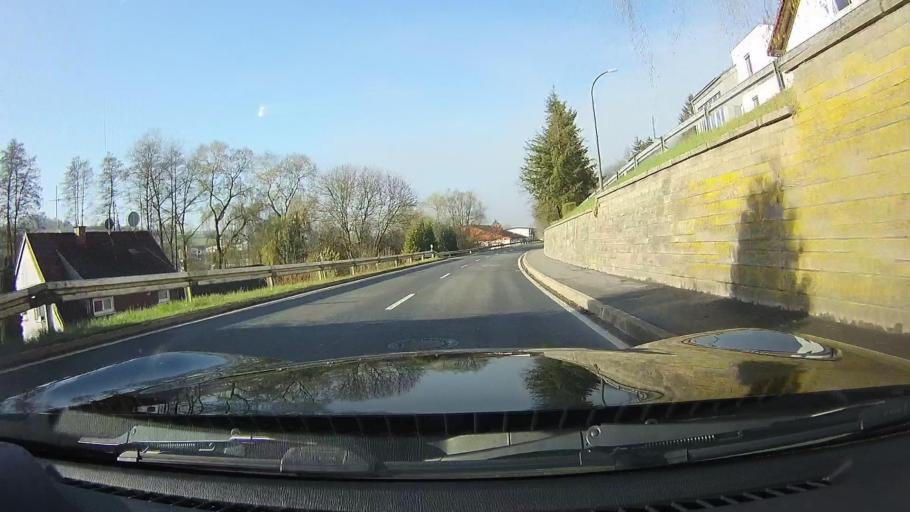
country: DE
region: Baden-Wuerttemberg
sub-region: Karlsruhe Region
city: Osterburken
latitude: 49.4247
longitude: 9.4145
